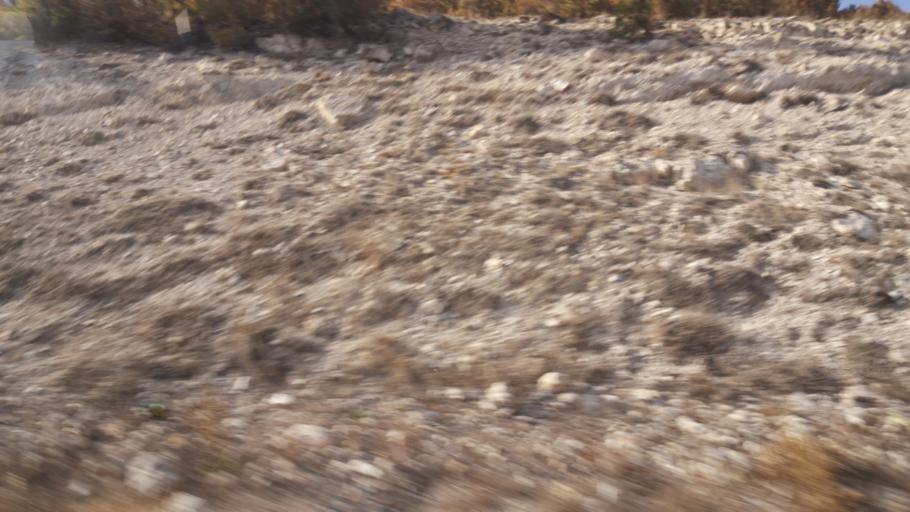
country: TR
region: Eskisehir
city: Kirka
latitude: 39.3468
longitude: 30.5866
